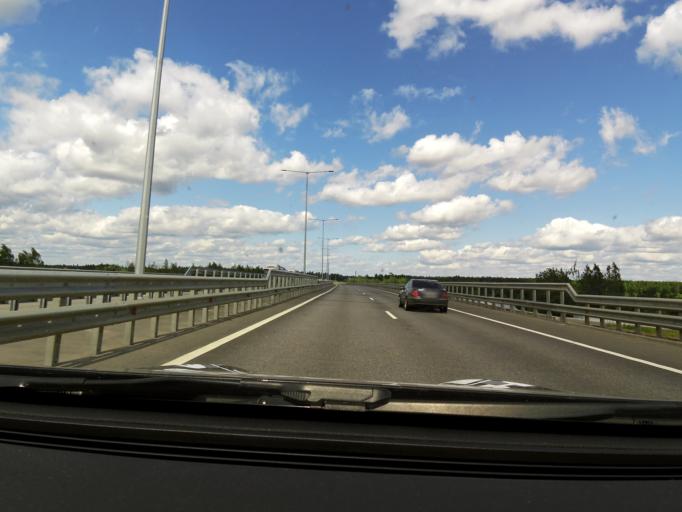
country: RU
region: Tverskaya
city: Vydropuzhsk
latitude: 57.2657
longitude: 34.8703
